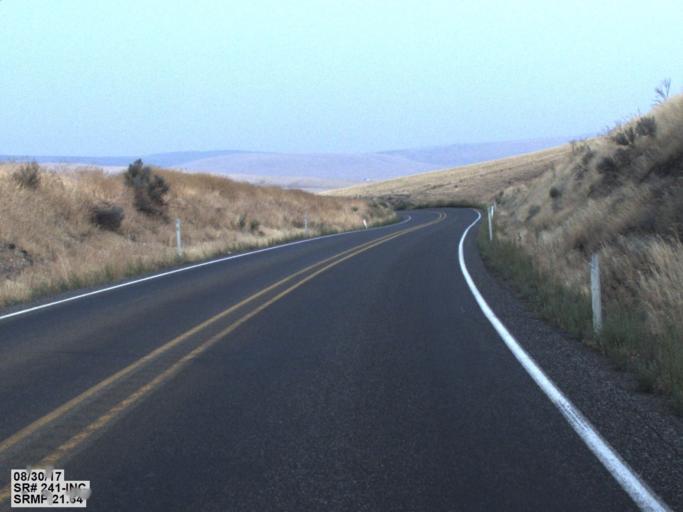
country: US
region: Washington
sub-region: Grant County
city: Desert Aire
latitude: 46.4943
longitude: -119.9049
